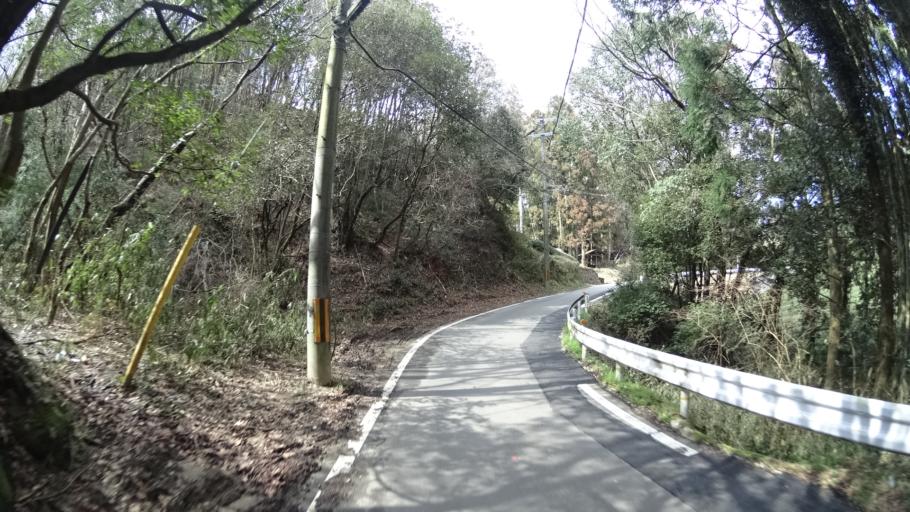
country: JP
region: Nara
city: Nara-shi
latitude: 34.7714
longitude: 135.9089
